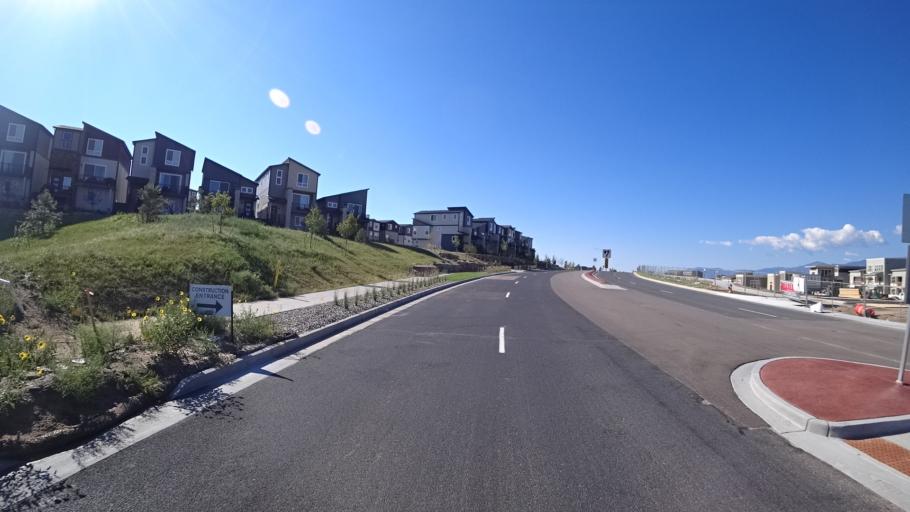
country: US
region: Colorado
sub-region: El Paso County
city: Gleneagle
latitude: 38.9959
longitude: -104.8036
